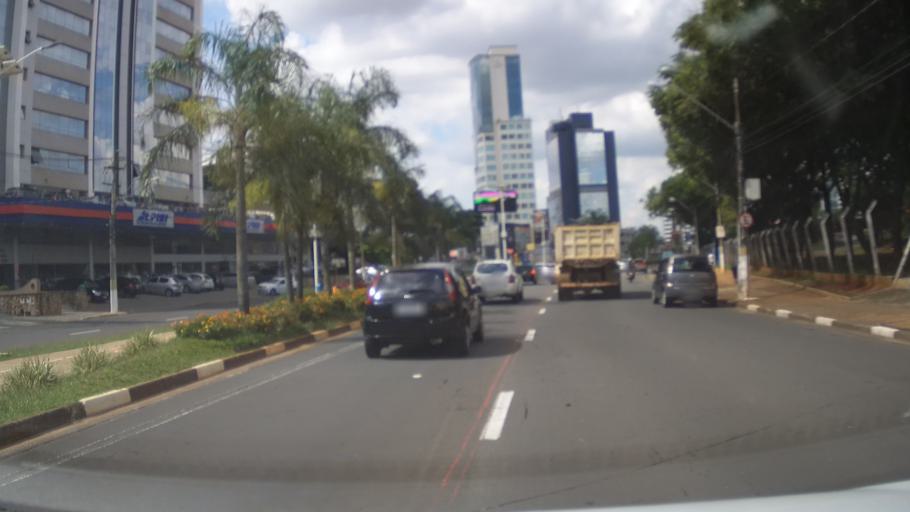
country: BR
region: Sao Paulo
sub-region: Campinas
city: Campinas
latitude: -22.8924
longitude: -47.0472
